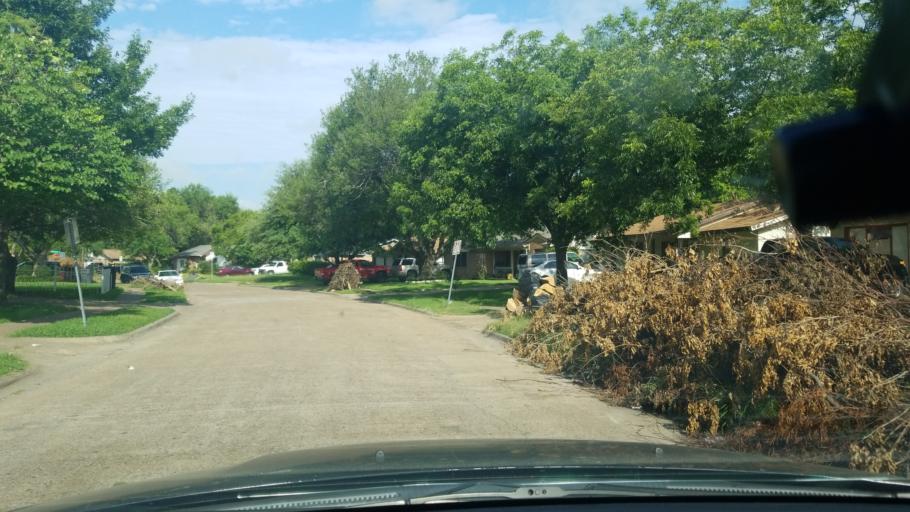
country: US
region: Texas
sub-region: Dallas County
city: Balch Springs
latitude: 32.7469
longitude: -96.6703
